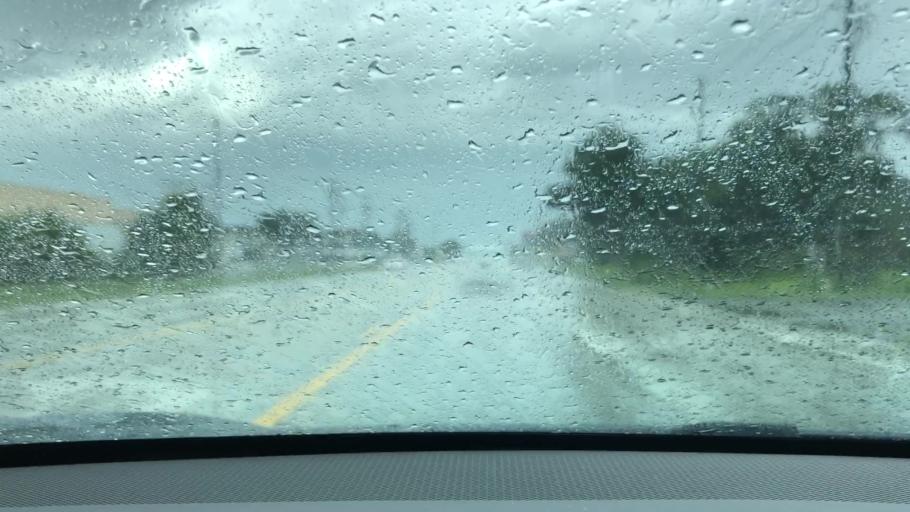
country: US
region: Florida
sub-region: Orange County
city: Belle Isle
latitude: 28.4562
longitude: -81.3651
